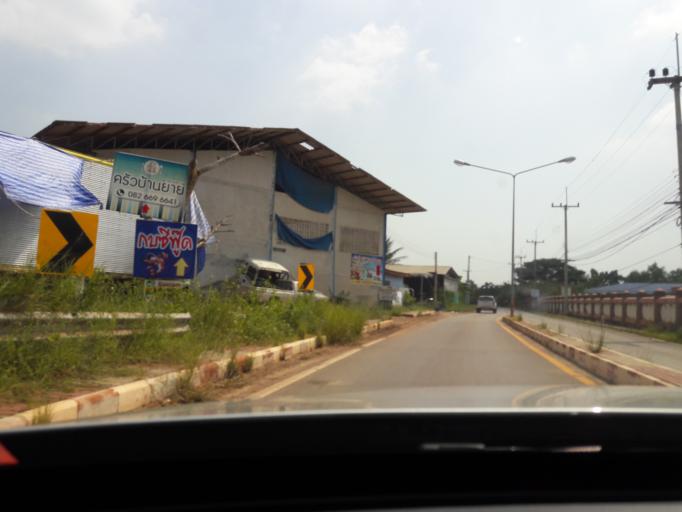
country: TH
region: Samut Songkhram
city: Amphawa
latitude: 13.3529
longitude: 99.9352
